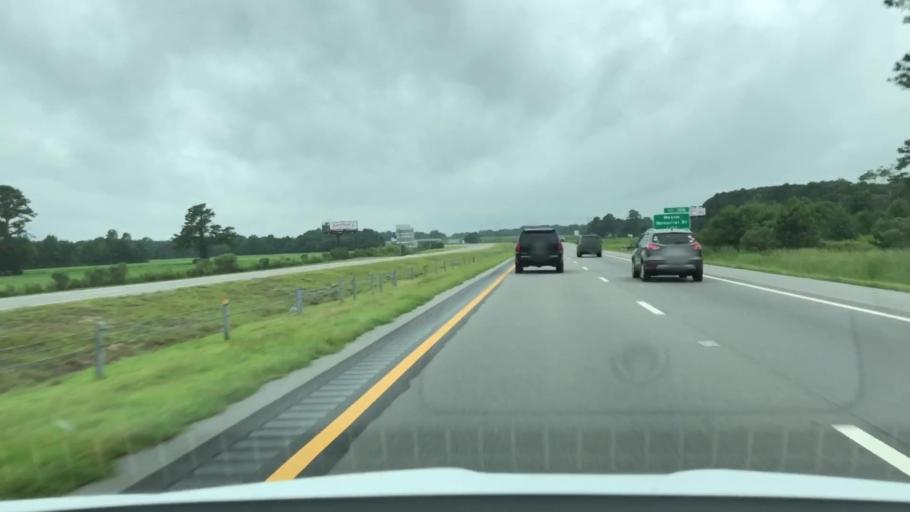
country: US
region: North Carolina
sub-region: Wayne County
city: Elroy
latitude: 35.4165
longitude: -77.9097
